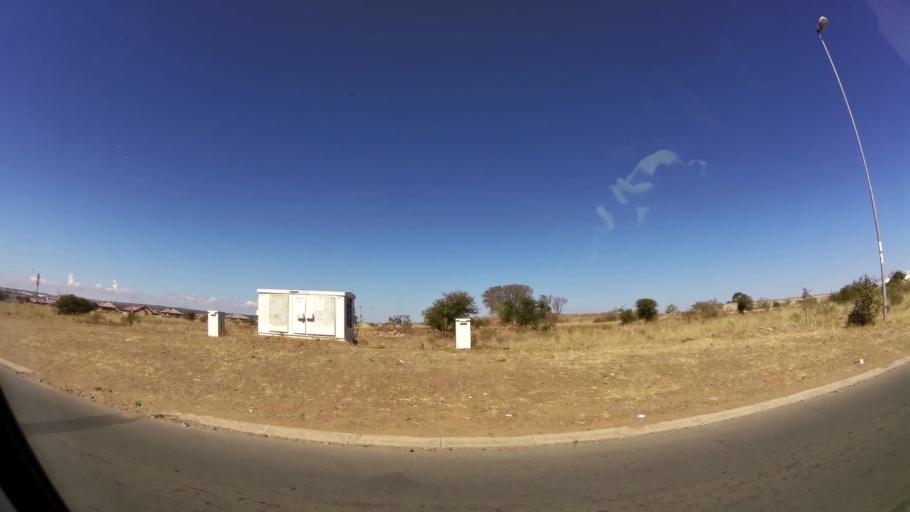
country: ZA
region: Limpopo
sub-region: Capricorn District Municipality
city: Polokwane
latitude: -23.8704
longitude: 29.4240
